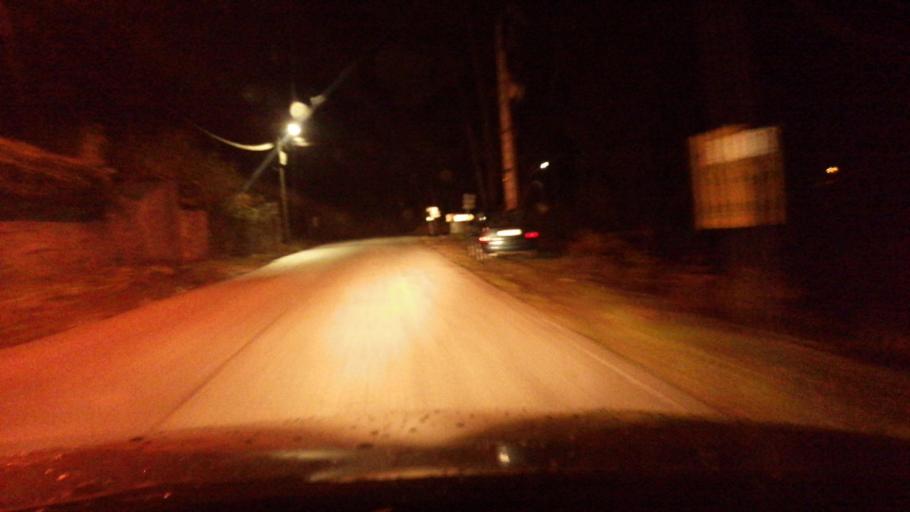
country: PT
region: Viseu
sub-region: Armamar
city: Armamar
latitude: 41.0547
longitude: -7.6416
